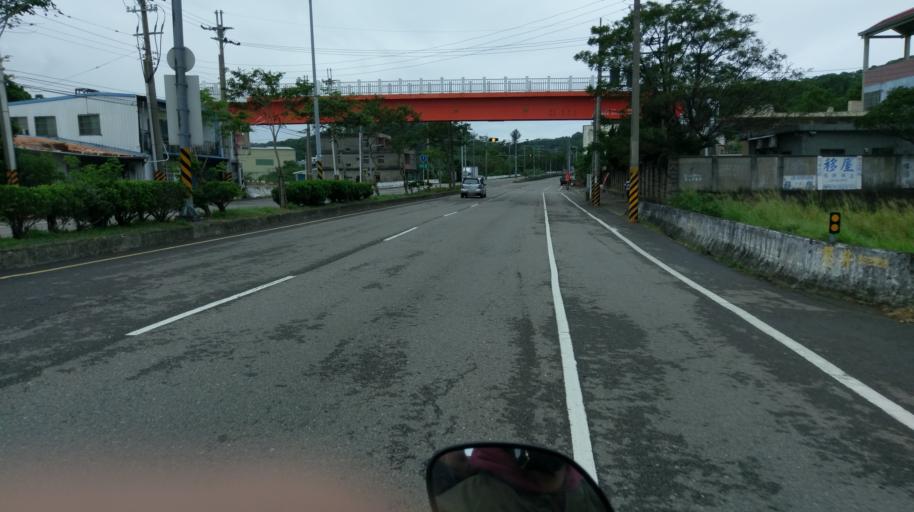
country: TW
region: Taiwan
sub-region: Miaoli
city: Miaoli
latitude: 24.6526
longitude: 120.8517
